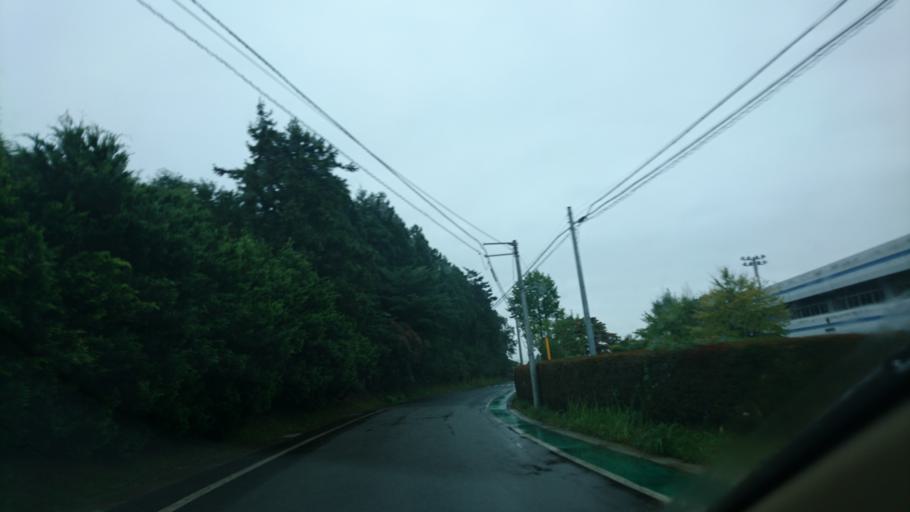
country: JP
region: Iwate
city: Mizusawa
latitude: 39.1348
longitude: 141.1913
